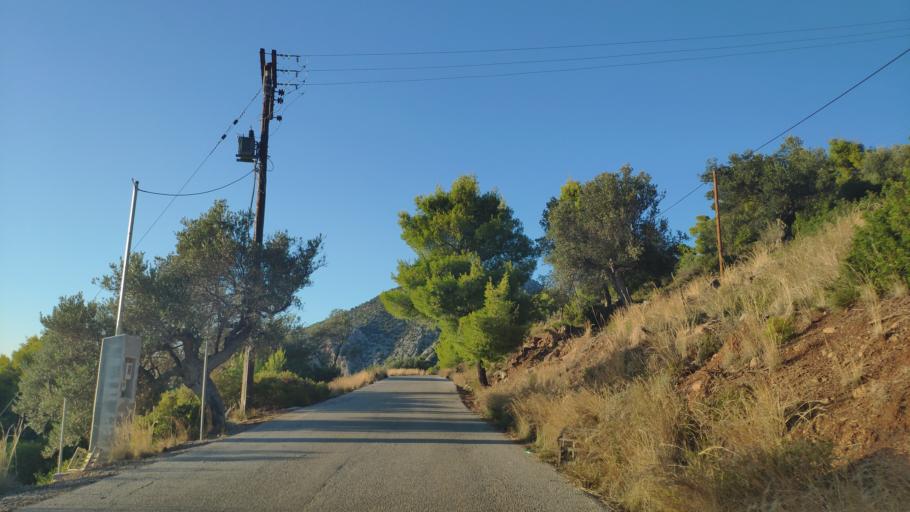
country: GR
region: Attica
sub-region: Nomos Piraios
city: Megalochori
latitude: 37.6031
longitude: 23.3307
